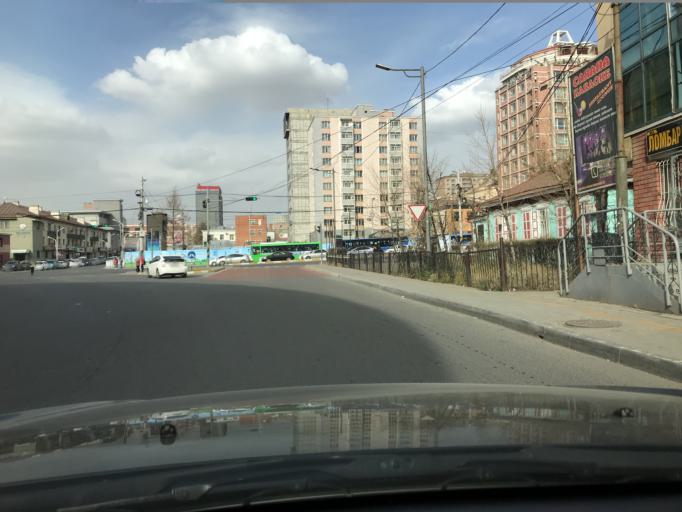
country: MN
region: Ulaanbaatar
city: Ulaanbaatar
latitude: 47.9179
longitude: 106.9358
